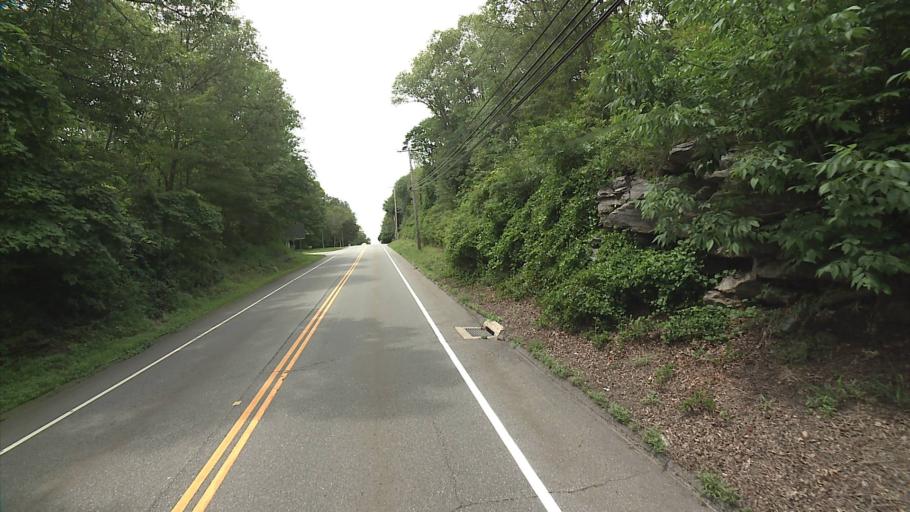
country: US
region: Connecticut
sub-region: New Haven County
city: Madison
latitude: 41.3583
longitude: -72.5675
